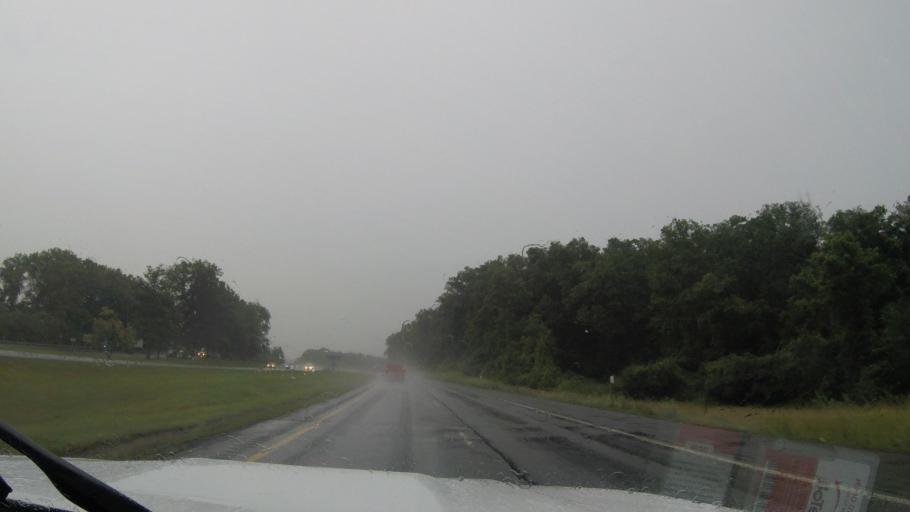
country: US
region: New York
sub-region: Seneca County
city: Seneca Falls
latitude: 42.9733
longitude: -76.8115
